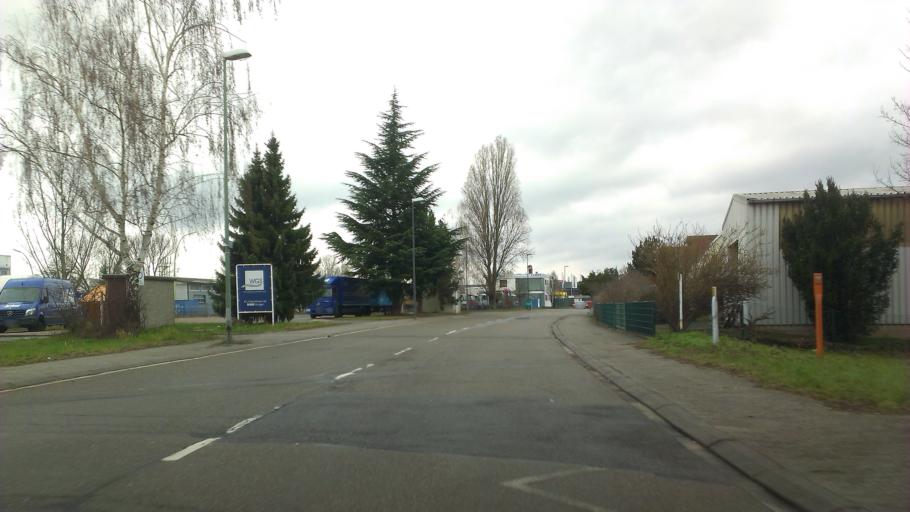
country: DE
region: Rheinland-Pfalz
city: Frankenthal
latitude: 49.4987
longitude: 8.3722
